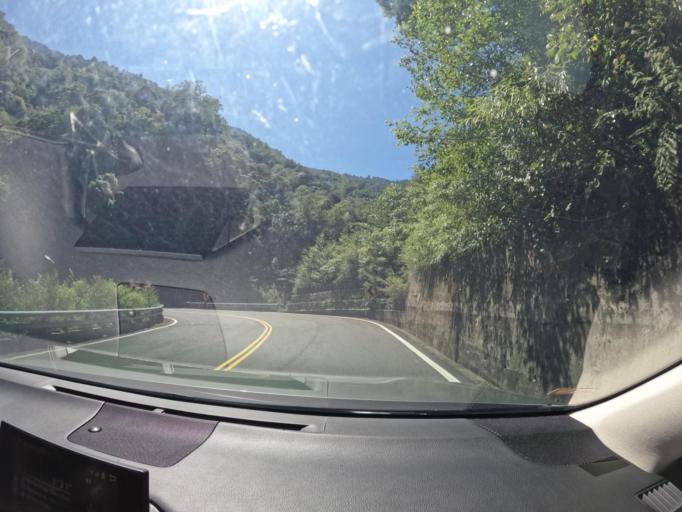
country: TW
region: Taiwan
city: Yujing
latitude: 23.2767
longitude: 120.8919
